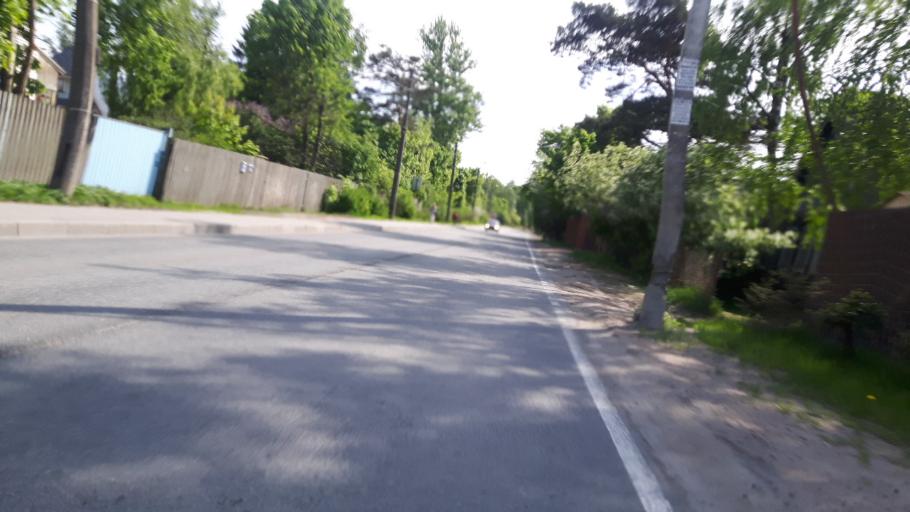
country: RU
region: Leningrad
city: Gorskaya
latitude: 60.0432
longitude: 29.9775
